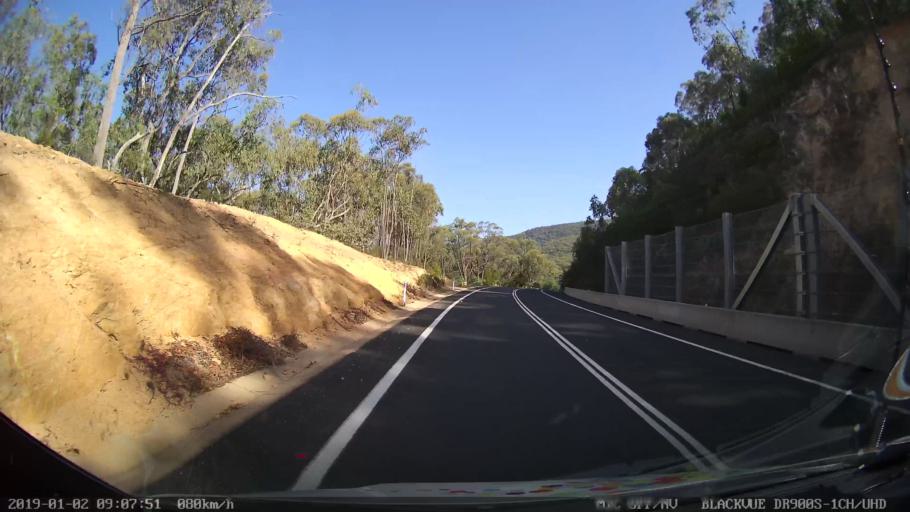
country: AU
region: New South Wales
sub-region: Tumut Shire
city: Tumut
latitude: -35.5363
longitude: 148.2957
